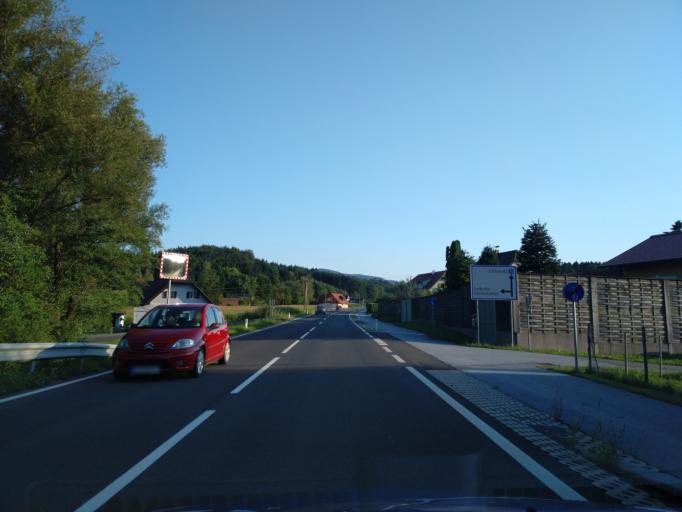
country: AT
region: Styria
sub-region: Politischer Bezirk Deutschlandsberg
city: Wies
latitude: 46.7145
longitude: 15.2528
